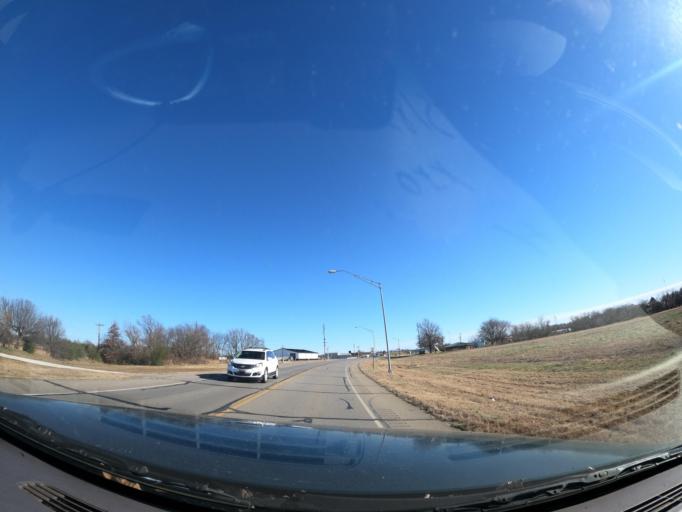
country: US
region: Oklahoma
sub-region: McIntosh County
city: Checotah
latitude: 35.4783
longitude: -95.5415
